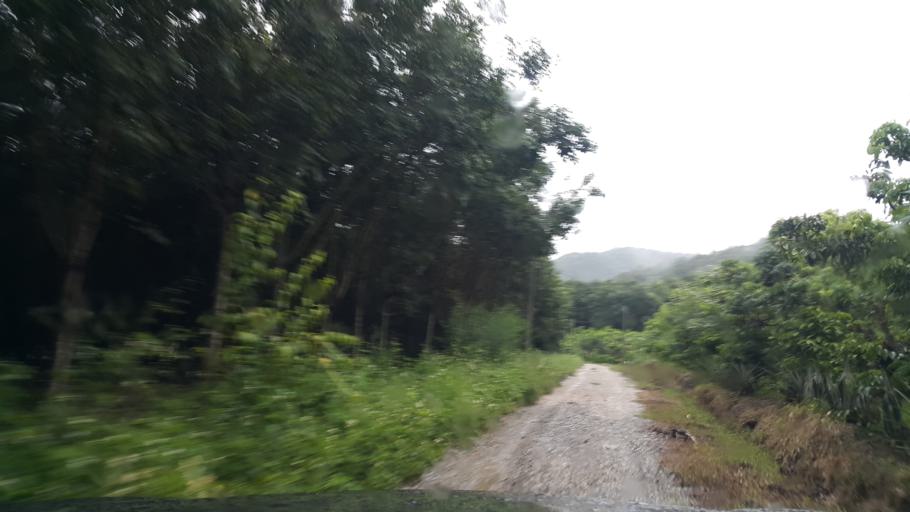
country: TH
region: Phayao
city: Phu Sang
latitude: 19.6202
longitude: 100.4071
